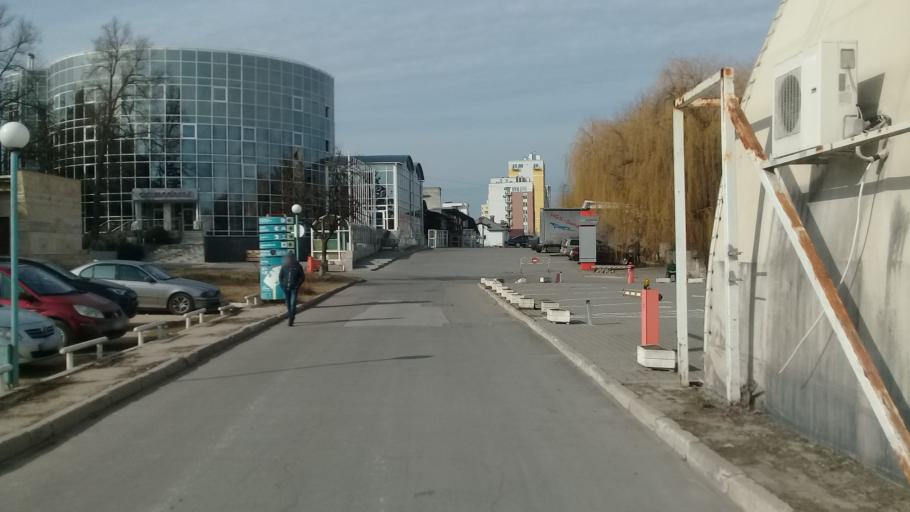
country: MD
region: Chisinau
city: Chisinau
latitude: 47.0171
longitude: 28.8020
